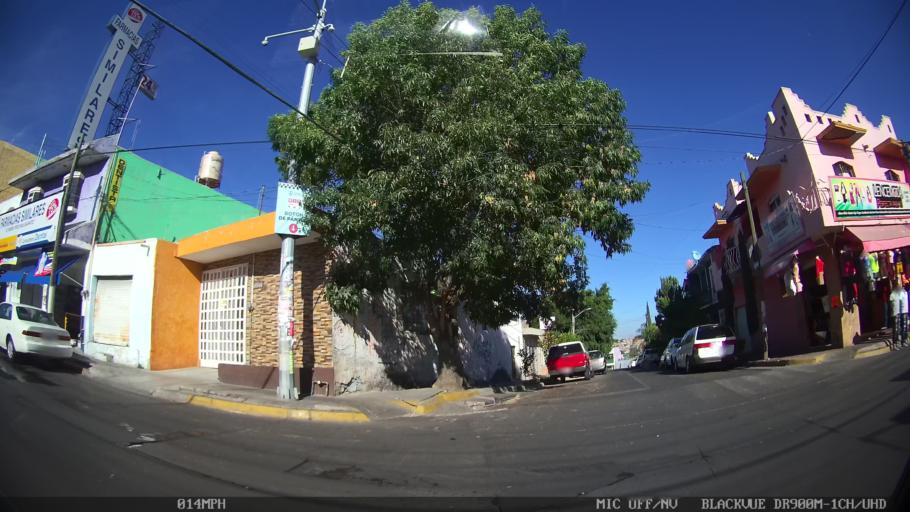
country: MX
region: Jalisco
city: Tlaquepaque
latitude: 20.6929
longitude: -103.2797
